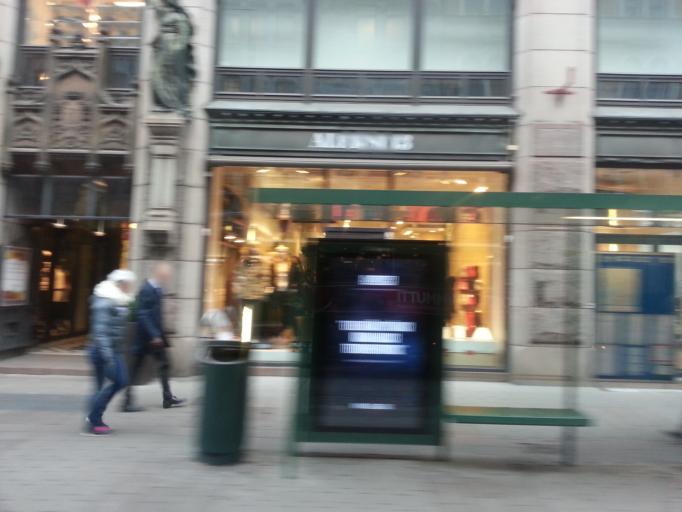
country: FI
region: Uusimaa
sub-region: Helsinki
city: Helsinki
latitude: 60.1689
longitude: 24.9460
